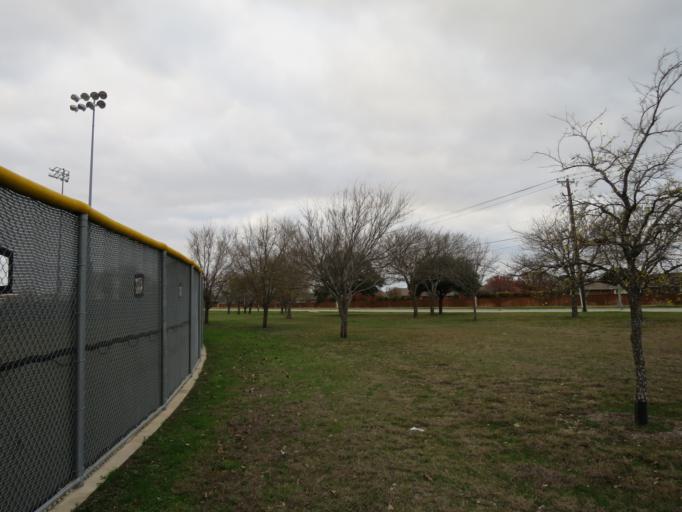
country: US
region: Texas
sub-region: Williamson County
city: Round Rock
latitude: 30.5461
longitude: -97.6187
